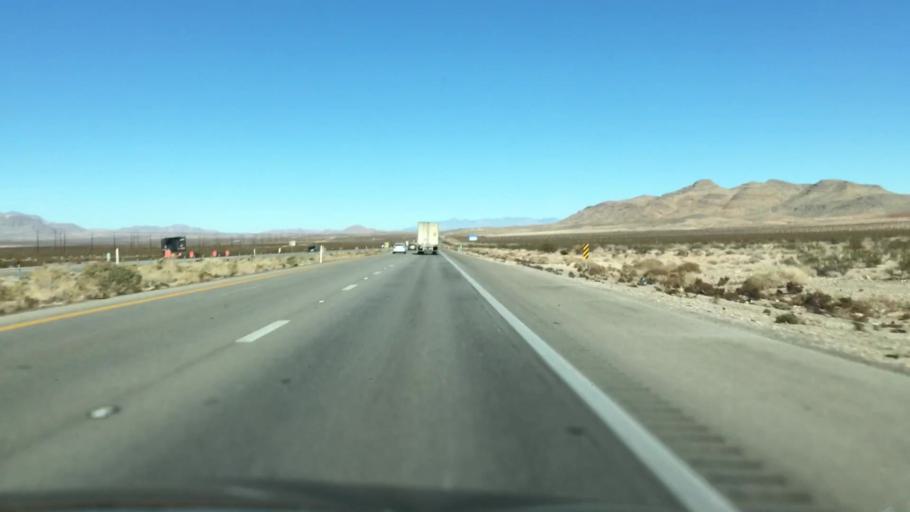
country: US
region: Nevada
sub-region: Clark County
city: Nellis Air Force Base
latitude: 36.4141
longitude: -114.8710
